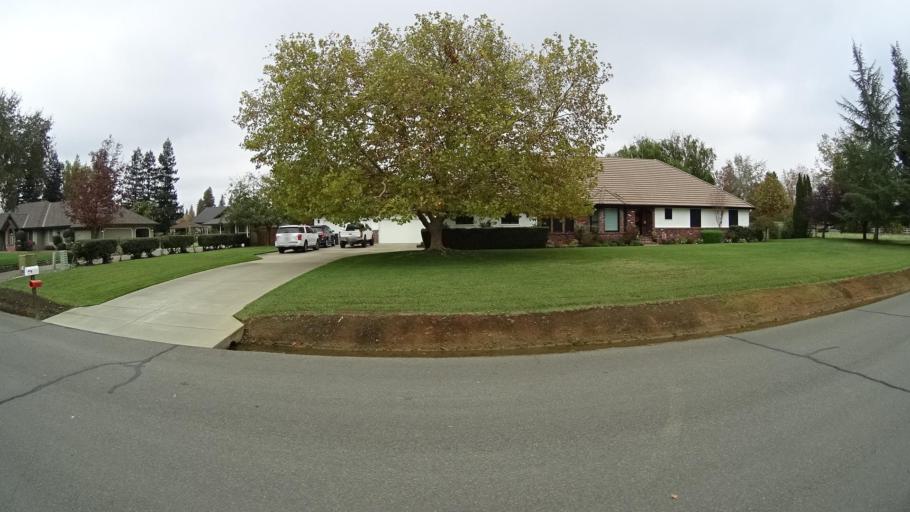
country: US
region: California
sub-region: Sacramento County
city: Vineyard
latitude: 38.4468
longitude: -121.3080
